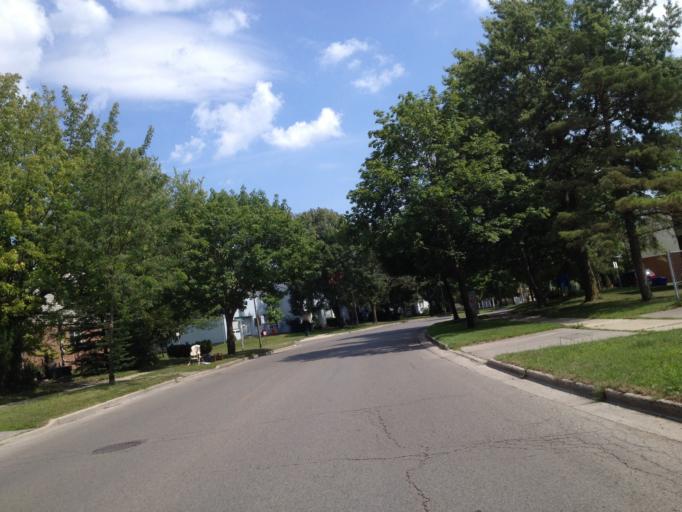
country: CA
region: Ontario
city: London
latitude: 43.0047
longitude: -81.3171
